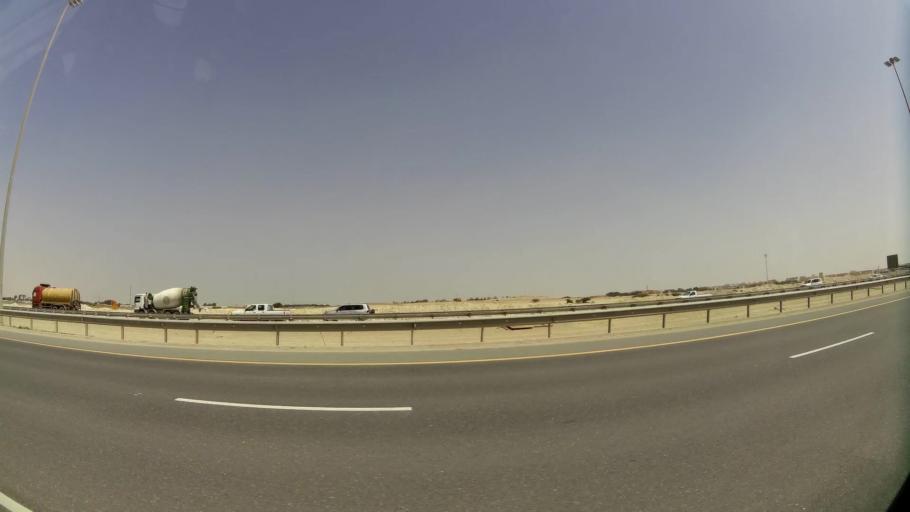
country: QA
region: Baladiyat Umm Salal
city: Umm Salal Muhammad
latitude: 25.4396
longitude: 51.4111
